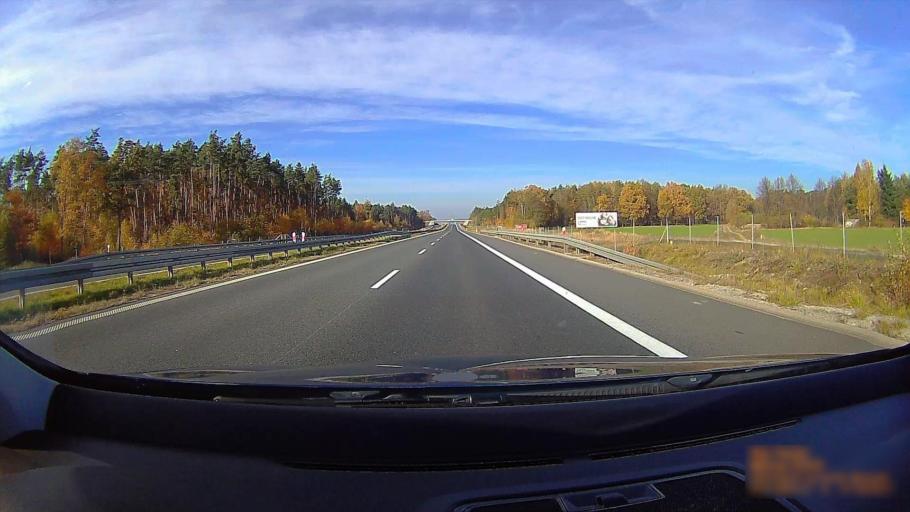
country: PL
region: Greater Poland Voivodeship
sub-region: Powiat ostrowski
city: Ostrow Wielkopolski
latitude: 51.6495
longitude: 17.8716
